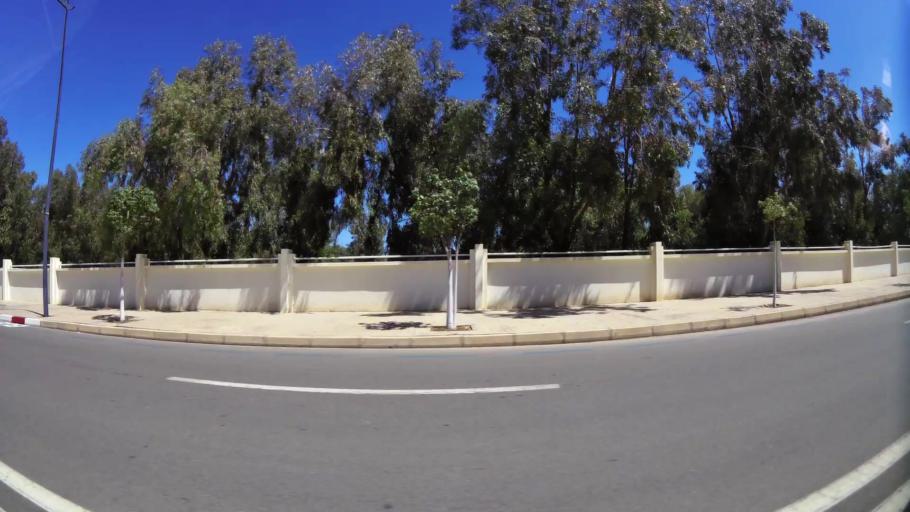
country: MA
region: Oriental
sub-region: Berkane-Taourirt
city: Madagh
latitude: 35.0902
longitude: -2.2478
